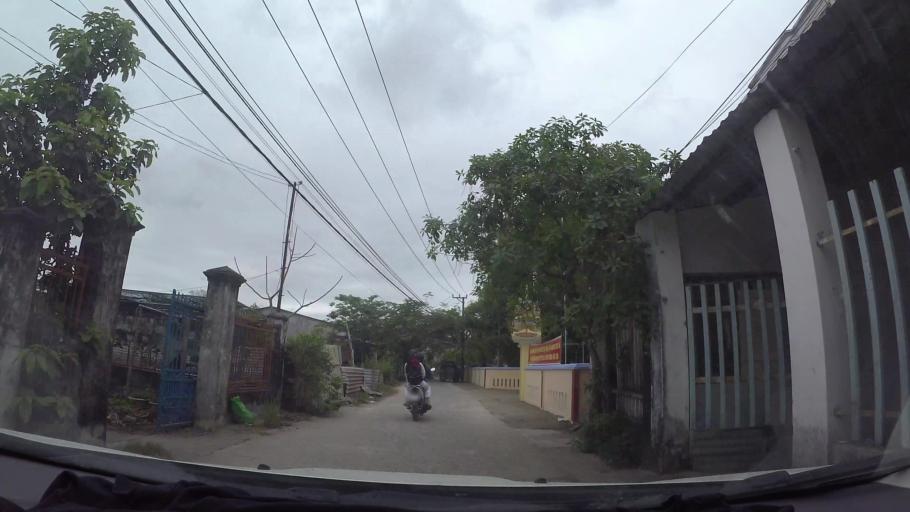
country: VN
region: Da Nang
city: Lien Chieu
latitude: 16.0883
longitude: 108.1023
